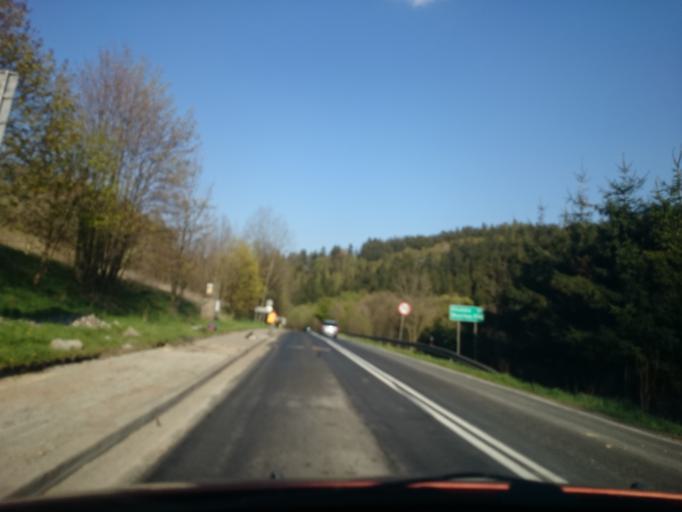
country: PL
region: Lower Silesian Voivodeship
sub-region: Powiat klodzki
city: Duszniki-Zdroj
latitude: 50.4043
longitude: 16.4021
